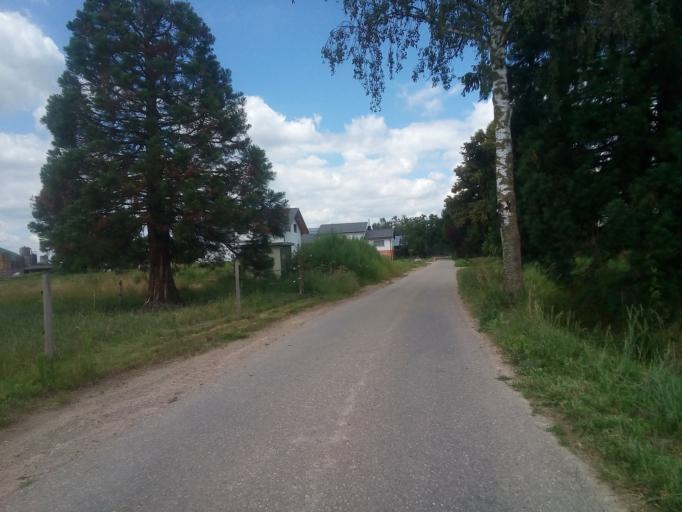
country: DE
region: Baden-Wuerttemberg
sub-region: Freiburg Region
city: Renchen
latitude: 48.6212
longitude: 7.9755
